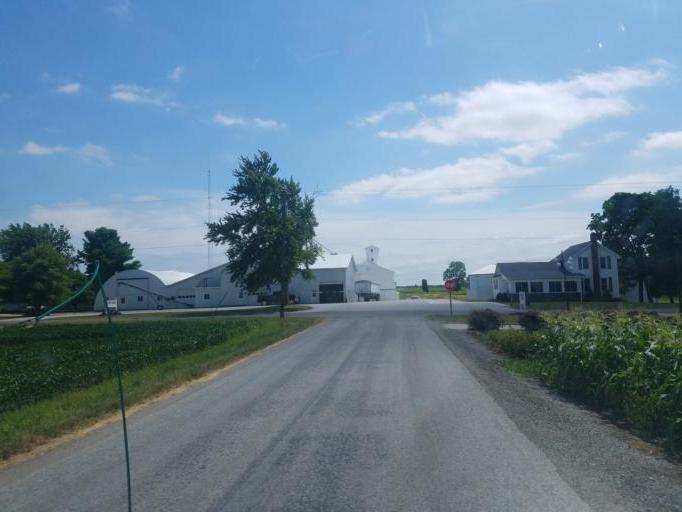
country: US
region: Indiana
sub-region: Allen County
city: Harlan
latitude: 41.1841
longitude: -84.8839
